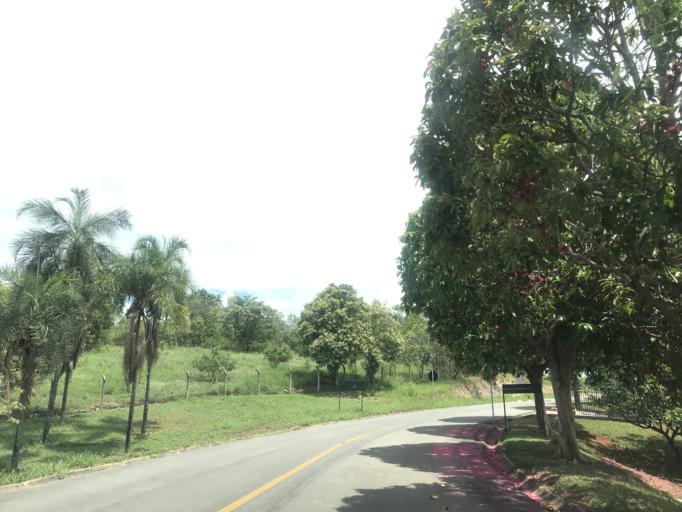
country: BR
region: Federal District
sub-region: Brasilia
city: Brasilia
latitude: -15.7975
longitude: -47.8000
